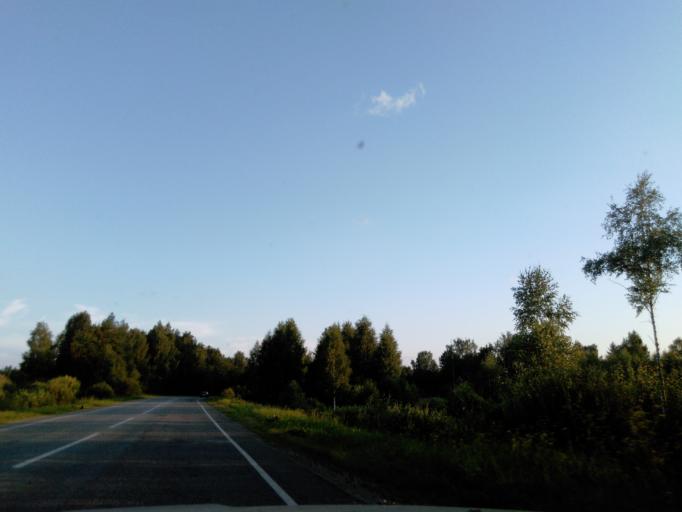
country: RU
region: Tverskaya
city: Konakovo
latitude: 56.6575
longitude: 36.7149
